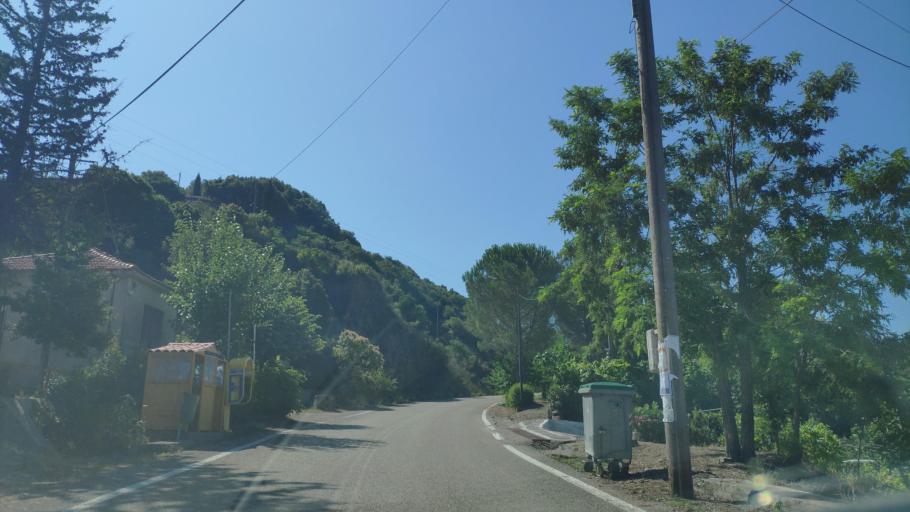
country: GR
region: West Greece
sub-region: Nomos Aitolias kai Akarnanias
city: Sardinia
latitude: 38.9264
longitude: 21.4087
